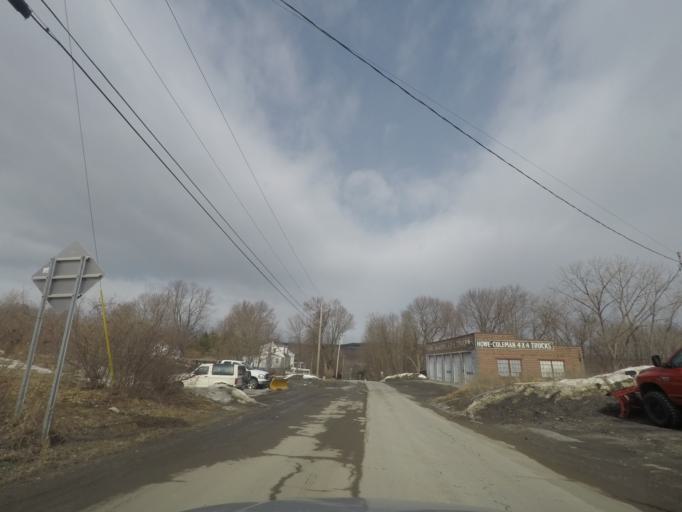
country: US
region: New York
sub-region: Rensselaer County
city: Wynantskill
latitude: 42.7581
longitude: -73.6153
